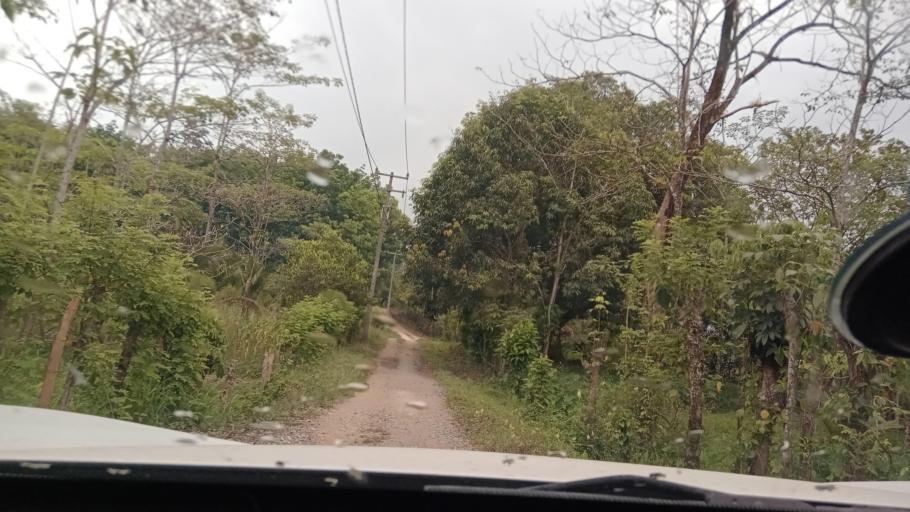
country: MX
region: Veracruz
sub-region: Uxpanapa
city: Poblado 10
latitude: 17.4506
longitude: -94.0903
